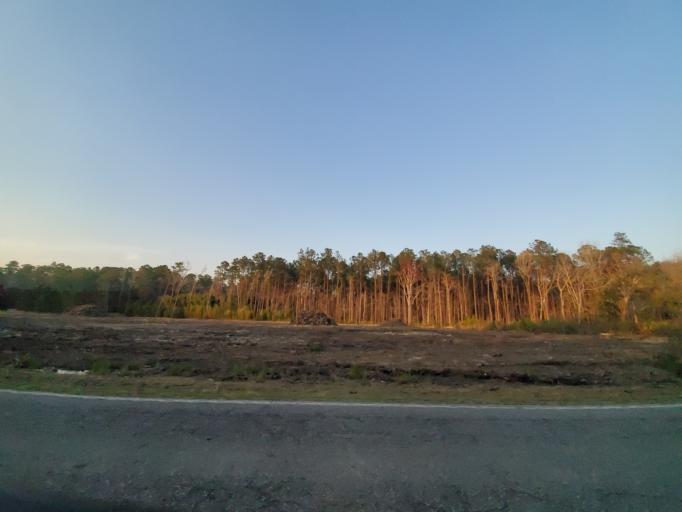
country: US
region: South Carolina
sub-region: Dorchester County
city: Ridgeville
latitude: 33.0249
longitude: -80.3844
